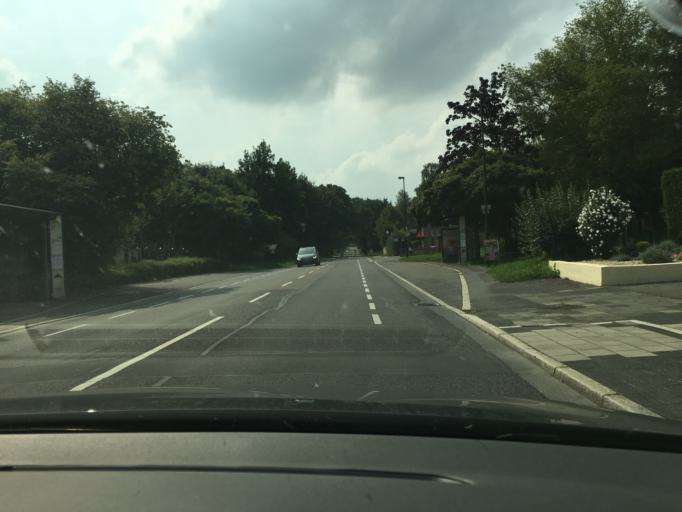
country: DE
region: North Rhine-Westphalia
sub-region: Regierungsbezirk Koln
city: Norvenich
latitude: 50.8516
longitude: 6.6271
